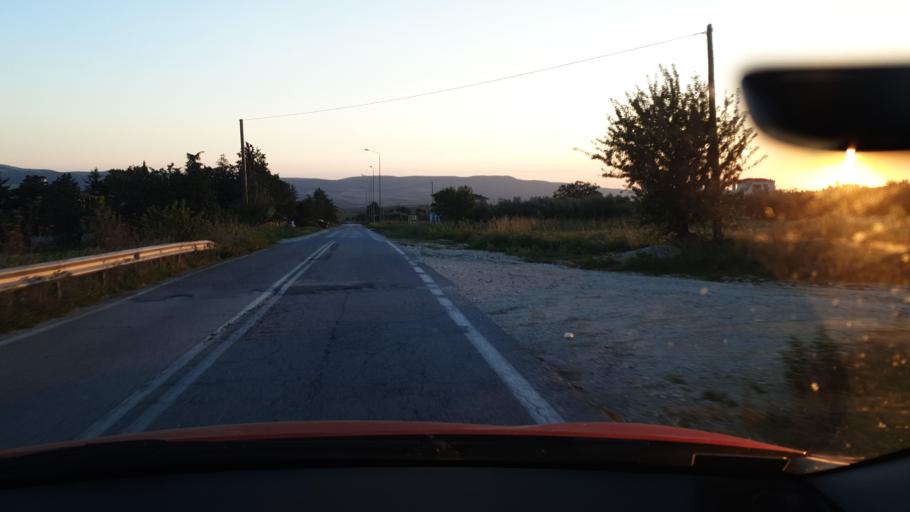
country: GR
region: Central Macedonia
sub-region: Nomos Chalkidikis
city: Galatista
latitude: 40.4693
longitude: 23.2519
